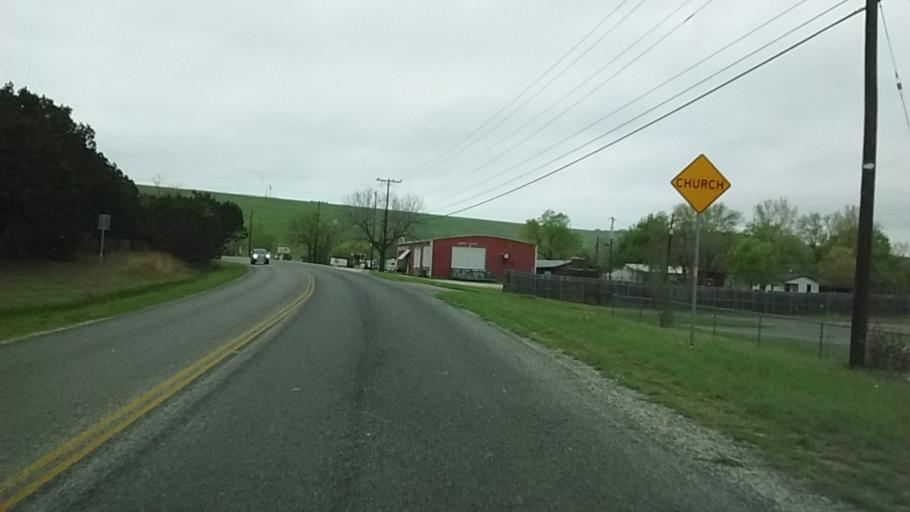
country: US
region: Texas
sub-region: Comal County
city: Canyon Lake
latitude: 29.8680
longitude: -98.1910
